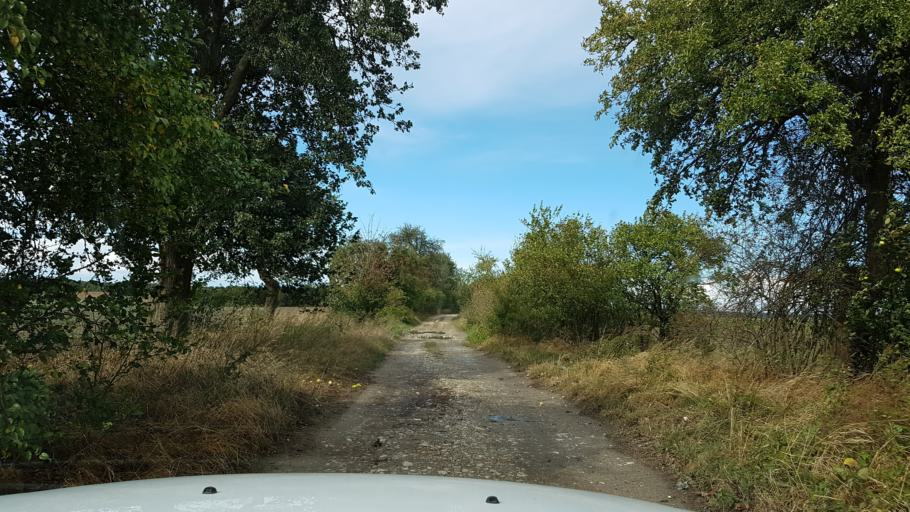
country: PL
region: West Pomeranian Voivodeship
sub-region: Powiat gryfinski
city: Banie
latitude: 53.1177
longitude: 14.6530
